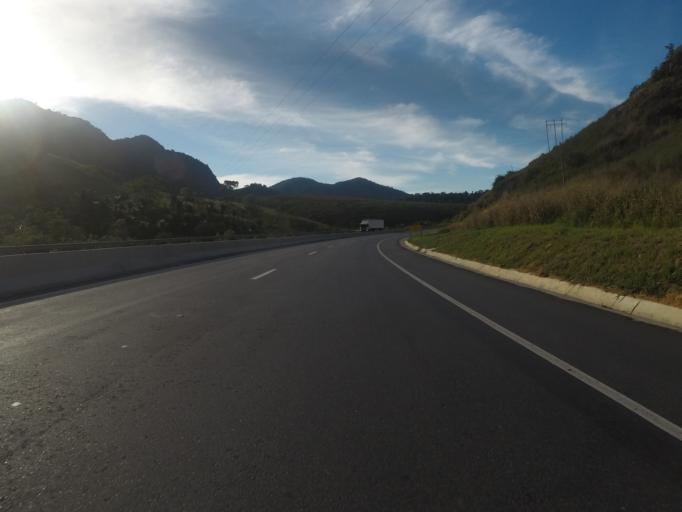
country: BR
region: Espirito Santo
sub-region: Ibiracu
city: Ibiracu
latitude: -19.8434
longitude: -40.3859
